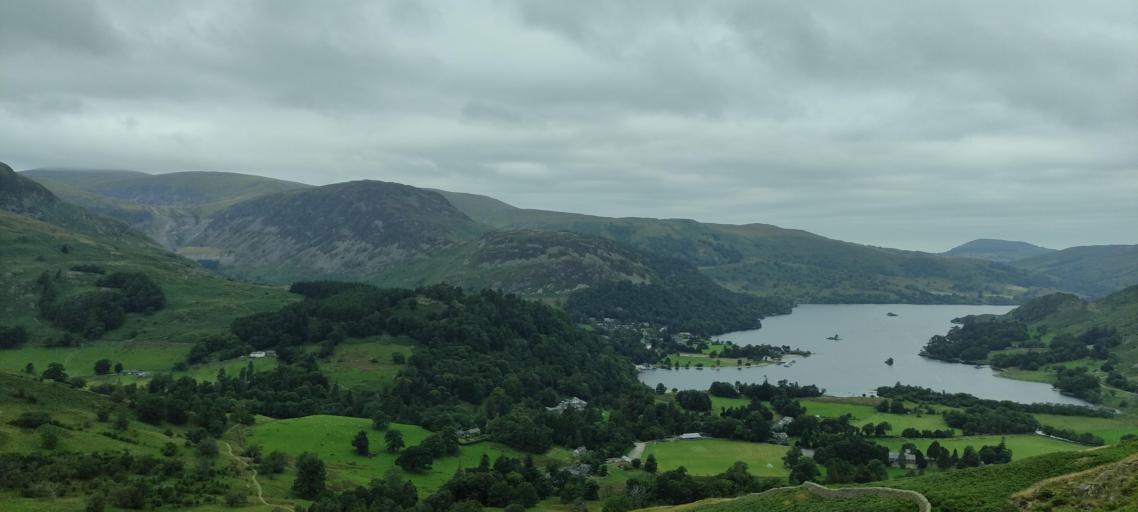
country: GB
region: England
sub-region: Cumbria
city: Ambleside
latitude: 54.5273
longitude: -2.9390
